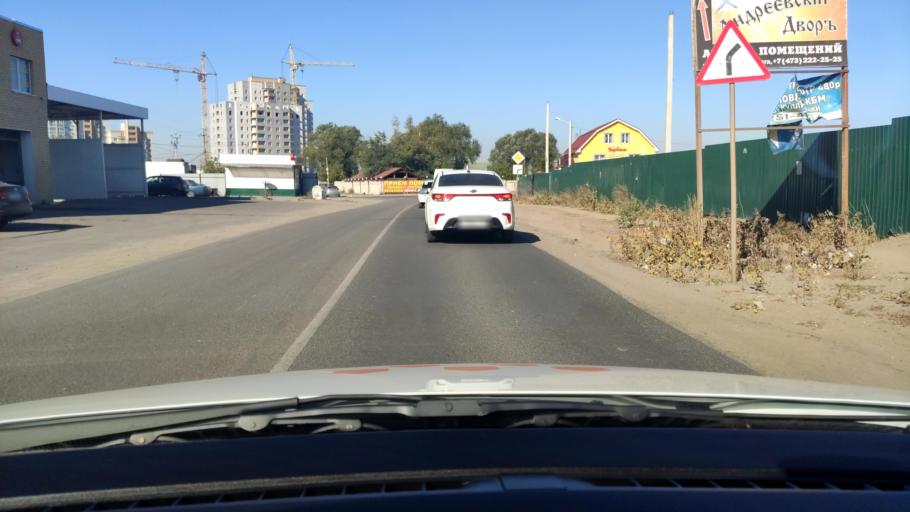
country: RU
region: Voronezj
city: Podgornoye
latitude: 51.7213
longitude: 39.1471
